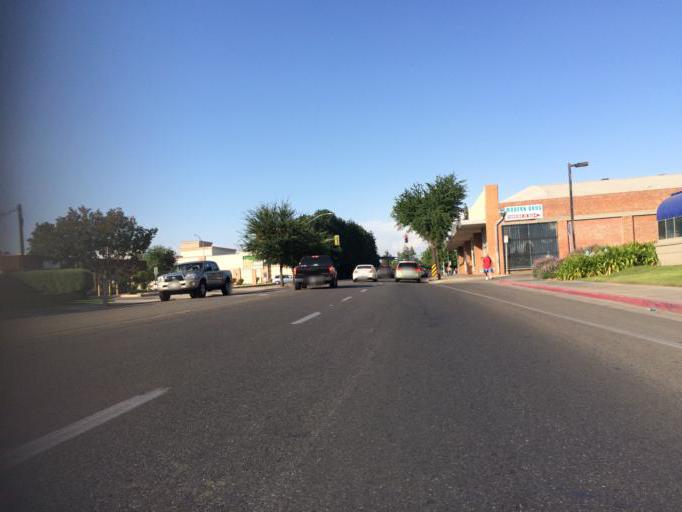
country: US
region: California
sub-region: Fresno County
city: Fresno
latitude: 36.7413
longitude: -119.7797
